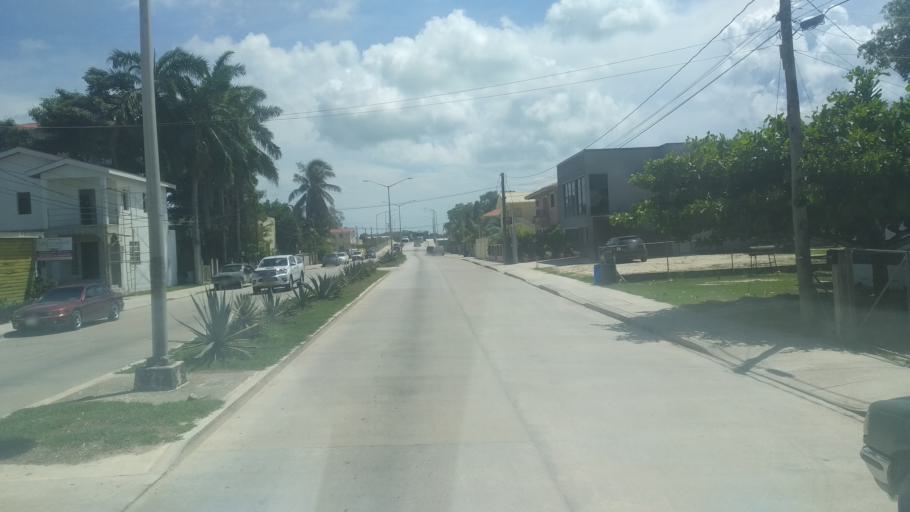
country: BZ
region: Belize
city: Belize City
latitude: 17.5099
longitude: -88.2215
